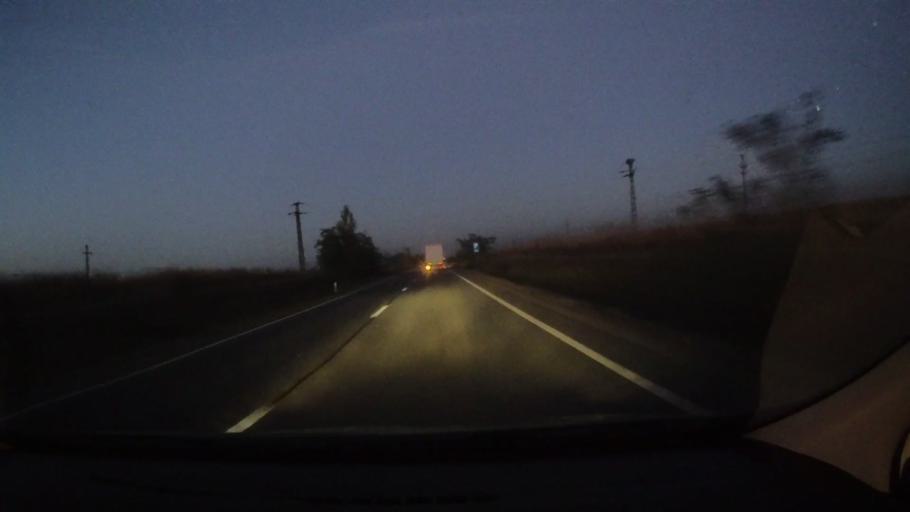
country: RO
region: Bihor
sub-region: Comuna Curtuiuseni
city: Curtuiseni
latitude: 47.5314
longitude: 22.1956
